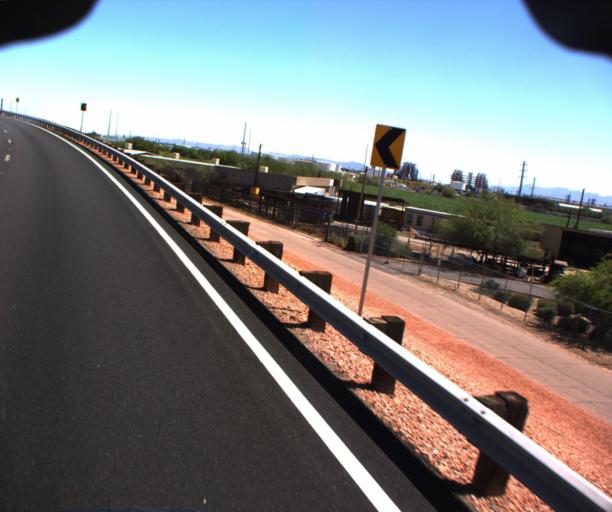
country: US
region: Arizona
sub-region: Maricopa County
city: Peoria
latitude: 33.5645
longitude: -112.2186
